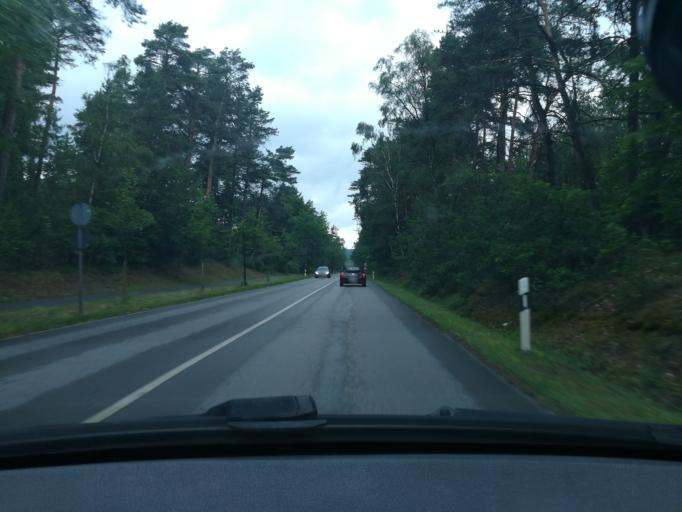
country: DE
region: North Rhine-Westphalia
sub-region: Regierungsbezirk Detmold
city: Oerlinghausen
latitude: 51.9234
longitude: 8.6554
